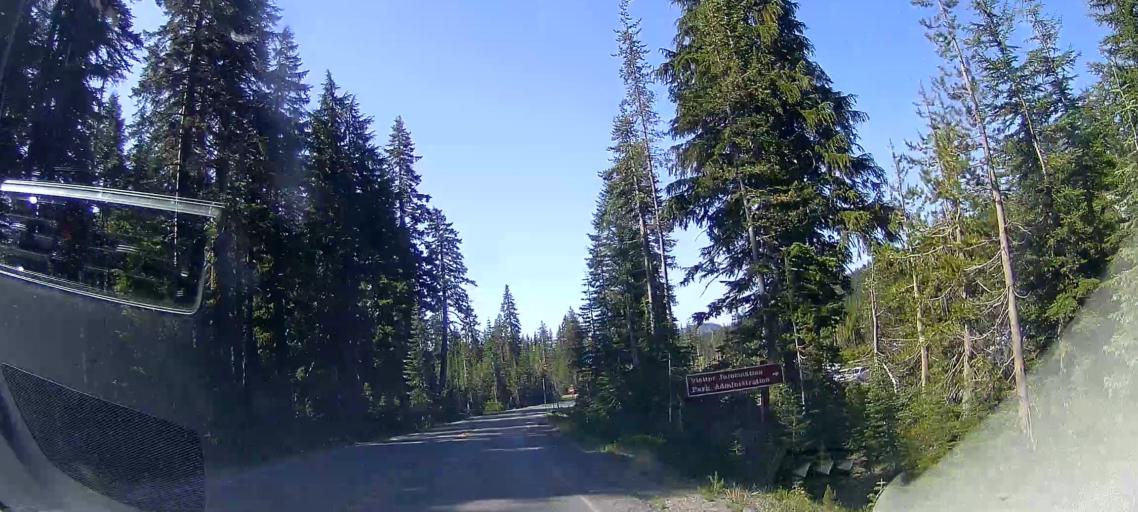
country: US
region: Oregon
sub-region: Jackson County
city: Shady Cove
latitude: 42.8974
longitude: -122.1331
